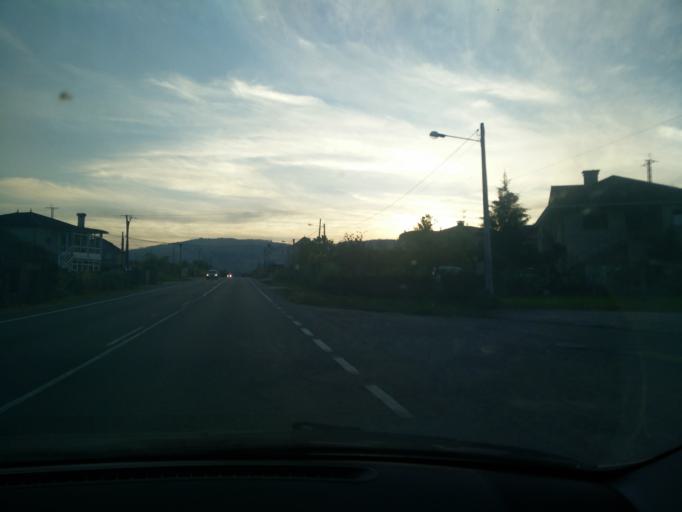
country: ES
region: Galicia
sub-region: Provincia de Pontevedra
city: Ponteareas
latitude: 42.1793
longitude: -8.5451
